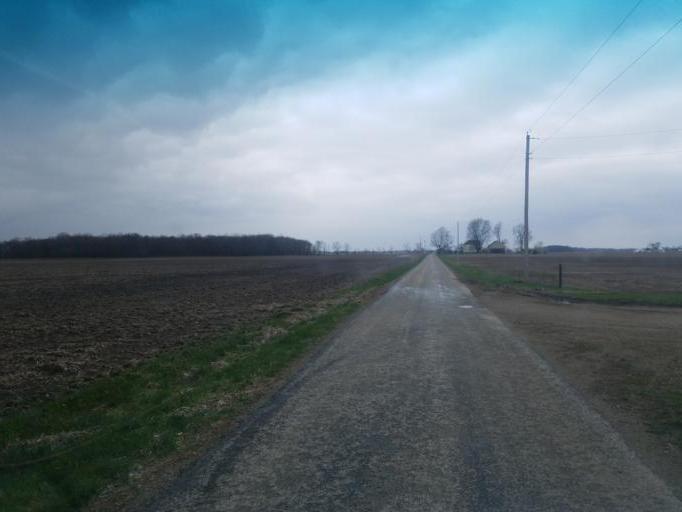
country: US
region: Ohio
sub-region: Marion County
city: Prospect
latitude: 40.4394
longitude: -83.1307
